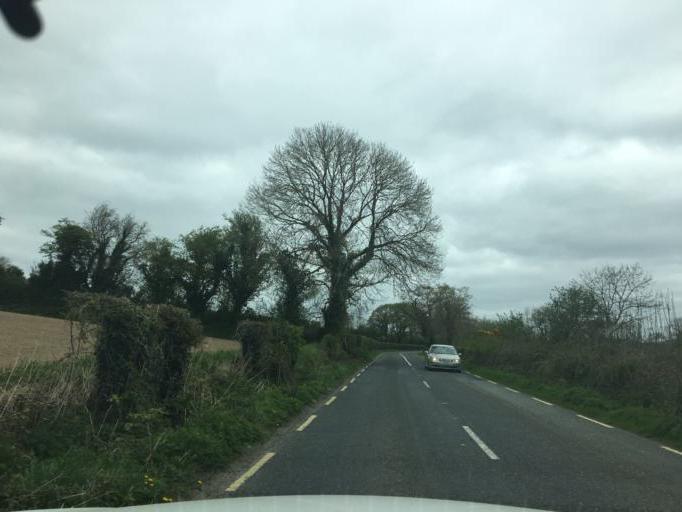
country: IE
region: Leinster
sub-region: Loch Garman
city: New Ross
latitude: 52.4423
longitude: -6.9712
